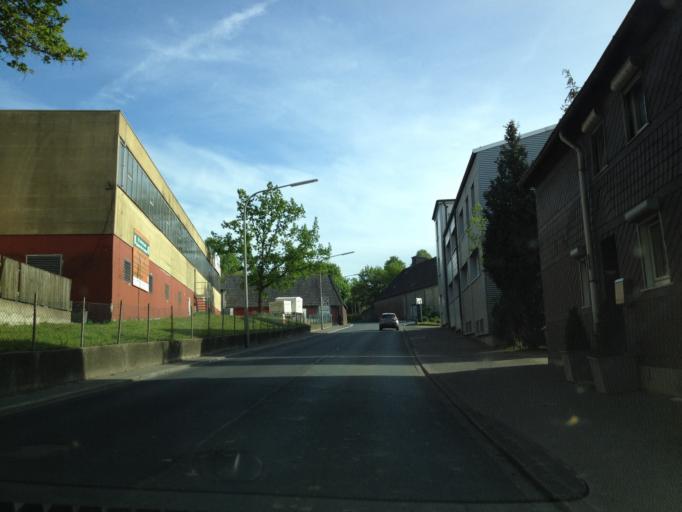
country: DE
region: North Rhine-Westphalia
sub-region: Regierungsbezirk Arnsberg
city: Werl
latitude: 51.4878
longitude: 7.9708
